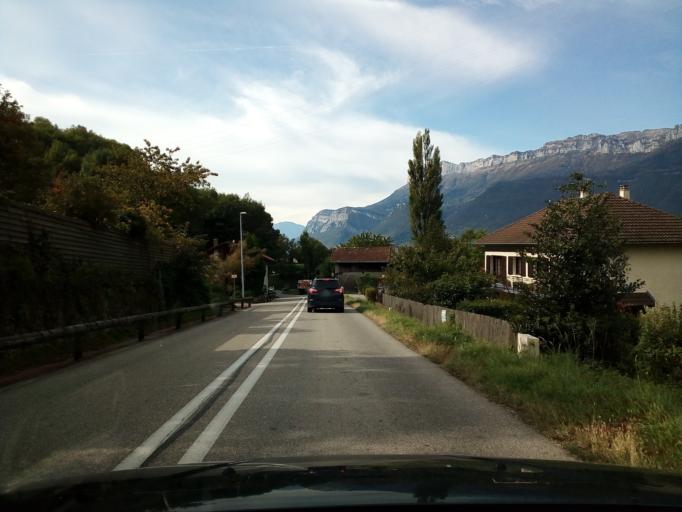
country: FR
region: Rhone-Alpes
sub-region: Departement de l'Isere
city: Le Cheylas
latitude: 45.3587
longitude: 5.9976
